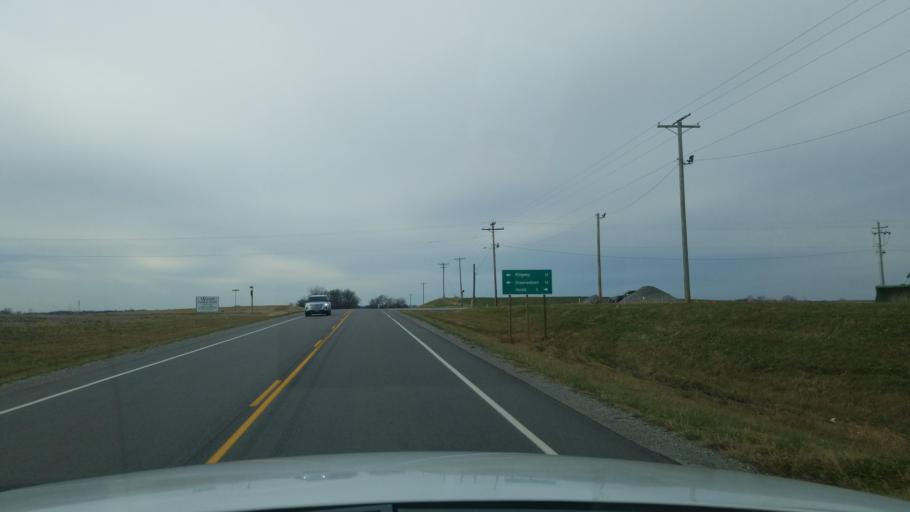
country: US
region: Illinois
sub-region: White County
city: Carmi
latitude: 37.9077
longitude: -88.1532
